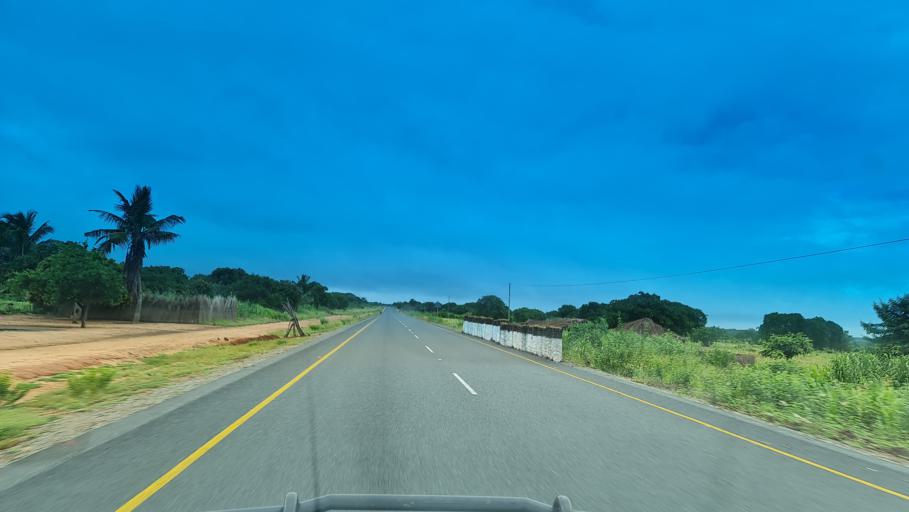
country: MZ
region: Nampula
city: Nampula
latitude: -15.5841
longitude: 39.3242
